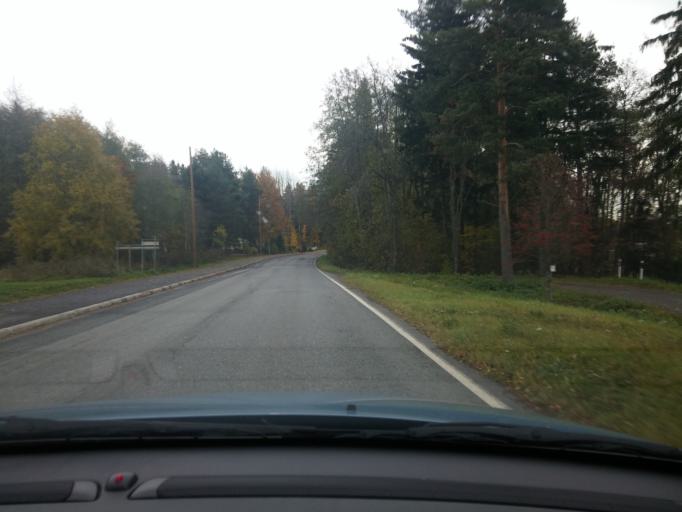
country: FI
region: Haeme
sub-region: Forssa
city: Tammela
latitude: 60.8052
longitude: 23.7988
